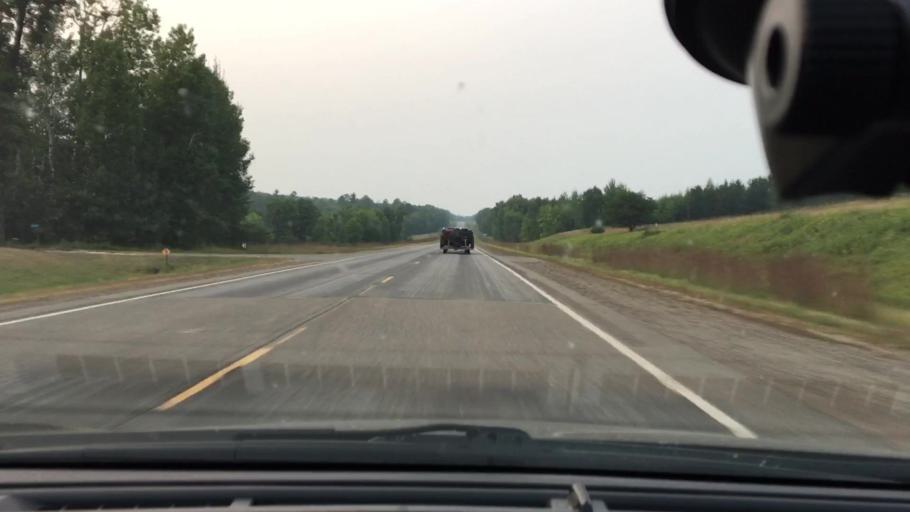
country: US
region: Minnesota
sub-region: Crow Wing County
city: Cross Lake
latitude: 46.6893
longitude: -93.9542
